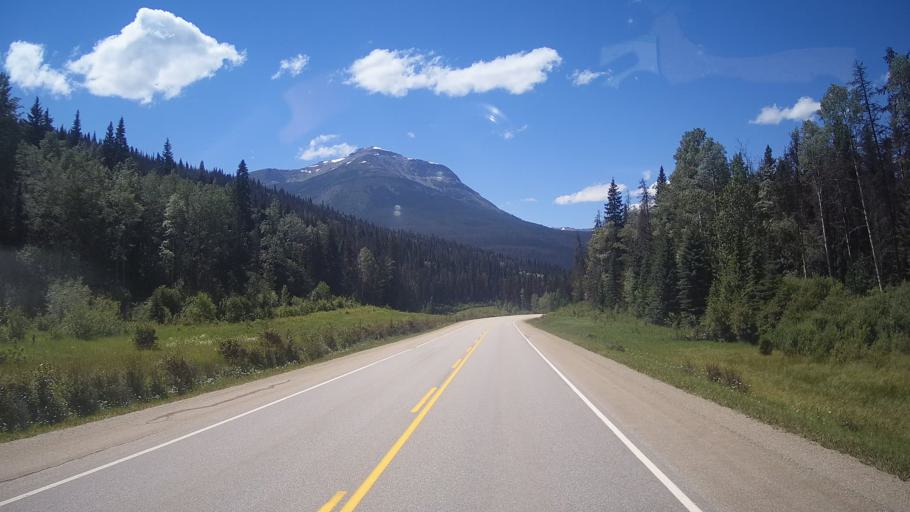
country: CA
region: Alberta
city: Jasper Park Lodge
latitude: 52.8497
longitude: -118.5665
